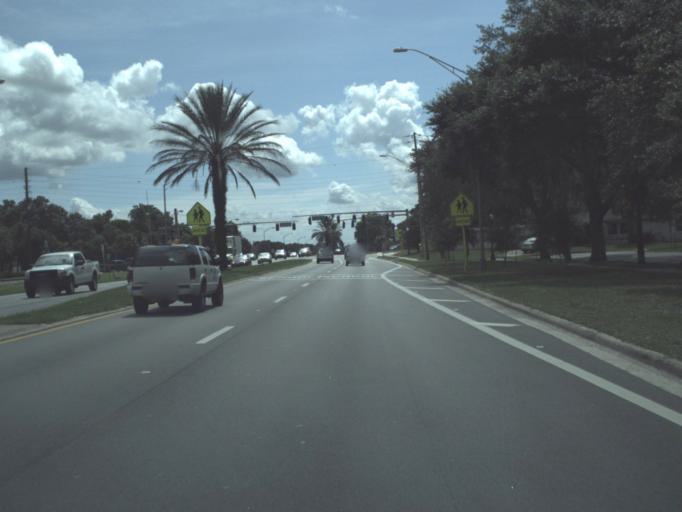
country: US
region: Florida
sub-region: Polk County
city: Lakeland
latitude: 28.0394
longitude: -81.9419
